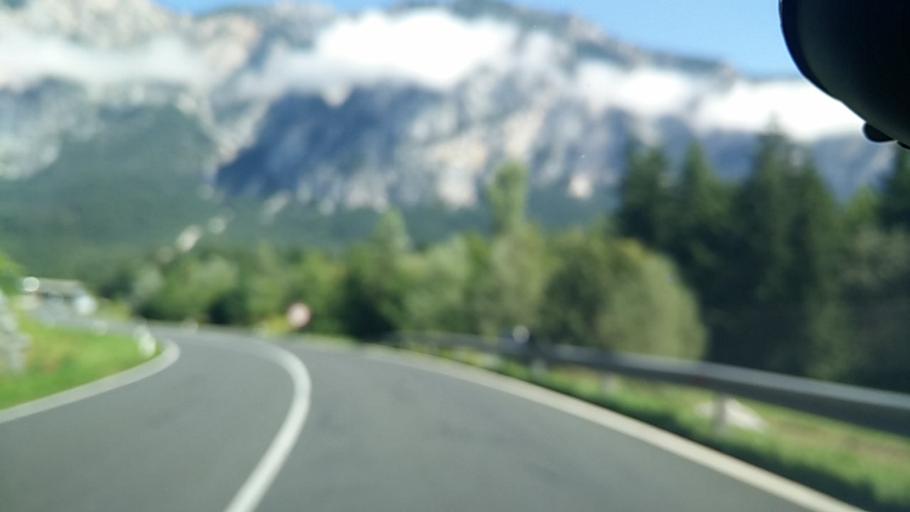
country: AT
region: Carinthia
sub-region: Politischer Bezirk Villach Land
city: Arnoldstein
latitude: 46.5653
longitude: 13.6954
